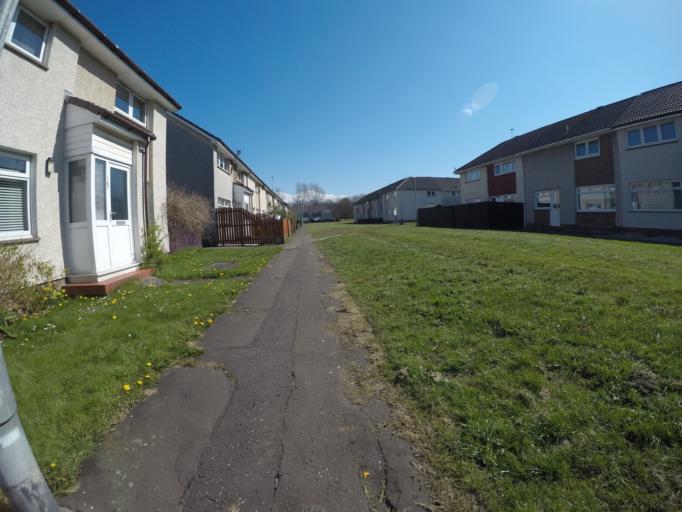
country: GB
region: Scotland
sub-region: North Ayrshire
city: Irvine
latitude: 55.6323
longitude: -4.6615
